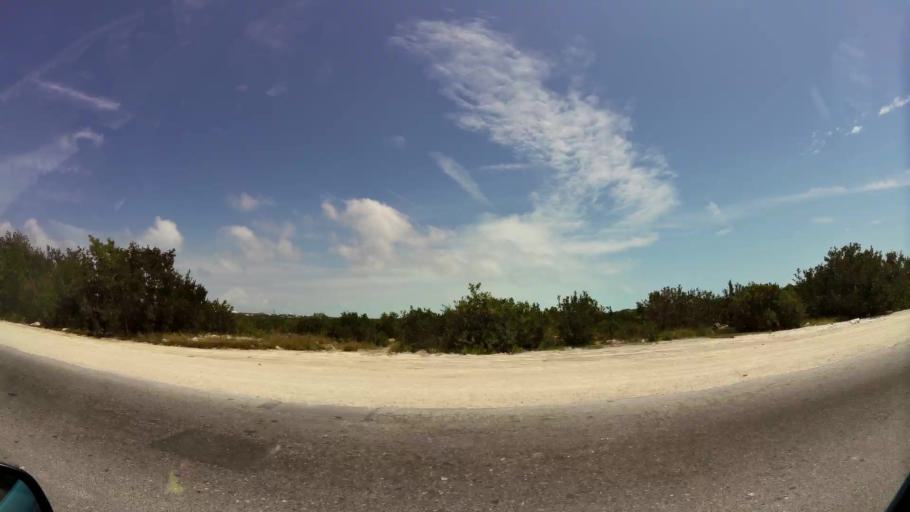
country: BS
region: Mayaguana
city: Abraham's Bay
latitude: 21.7726
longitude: -72.2521
